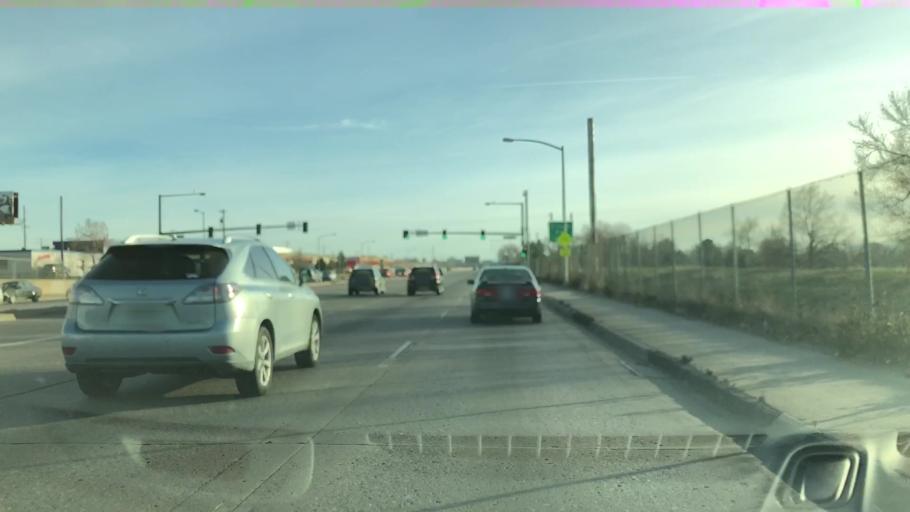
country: US
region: Colorado
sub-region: Arapahoe County
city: Englewood
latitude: 39.6885
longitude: -104.9922
